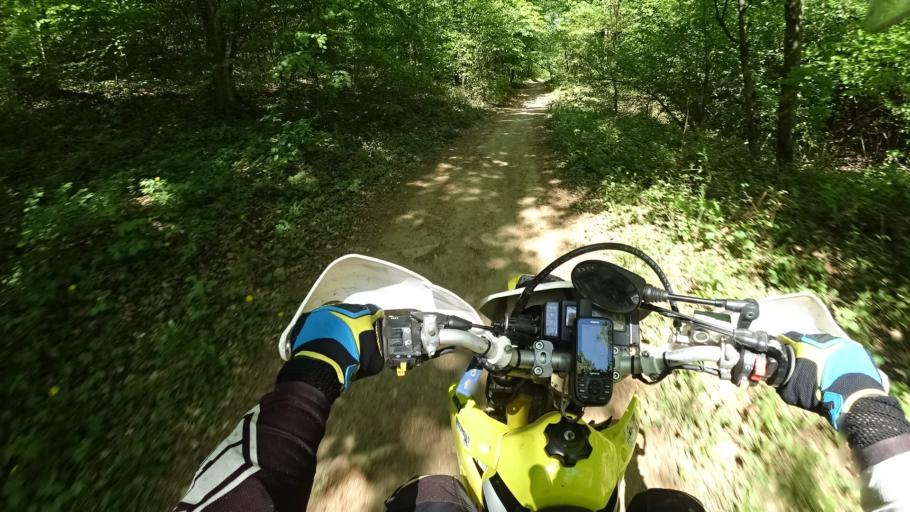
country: HR
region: Zagrebacka
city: Jablanovec
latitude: 45.8675
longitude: 15.8542
